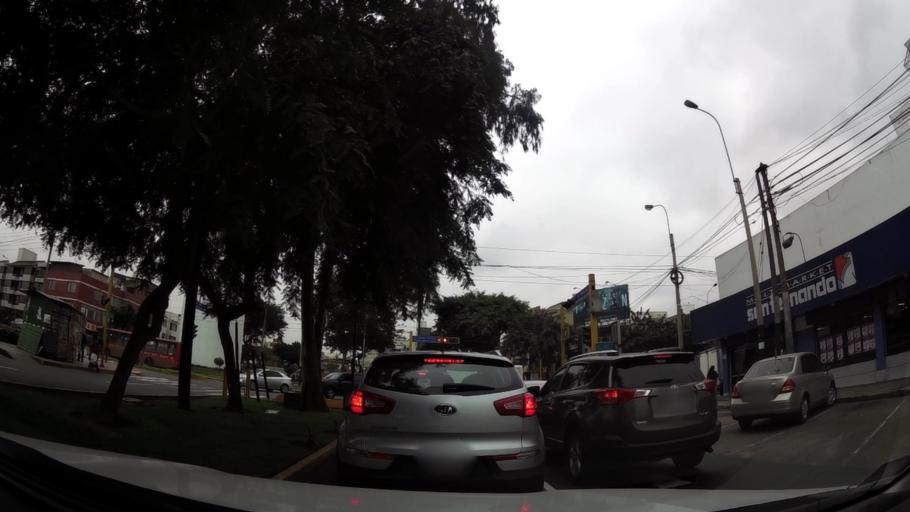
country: PE
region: Lima
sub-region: Lima
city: Surco
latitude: -12.1208
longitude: -76.9882
